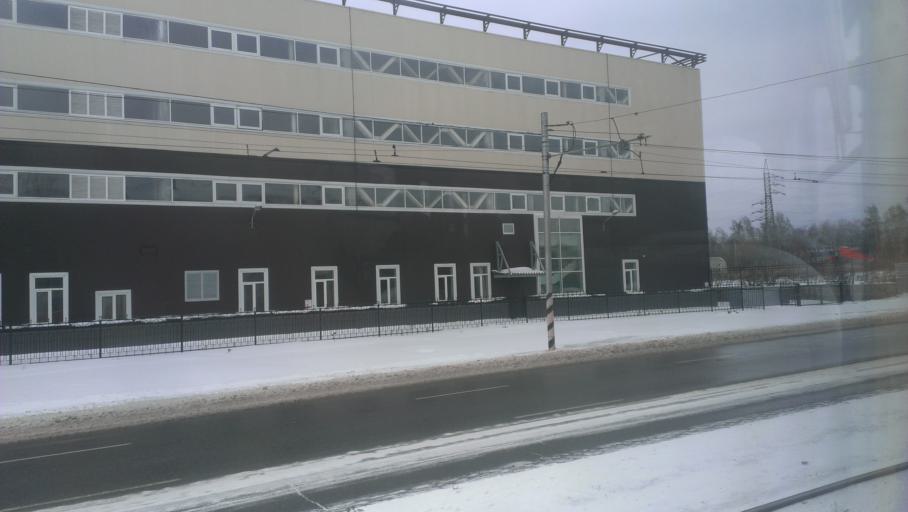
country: RU
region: Altai Krai
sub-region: Gorod Barnaulskiy
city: Barnaul
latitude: 53.3843
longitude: 83.7130
